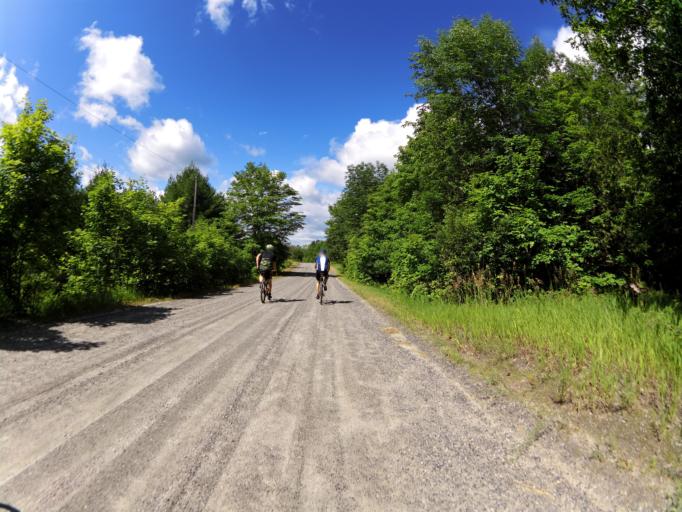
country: CA
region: Ontario
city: Perth
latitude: 45.0791
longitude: -76.4548
